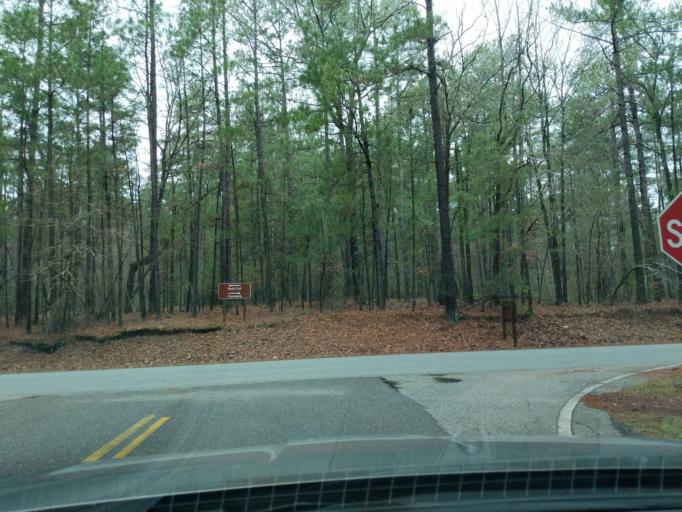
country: US
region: Georgia
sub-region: Columbia County
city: Appling
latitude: 33.6468
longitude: -82.3870
